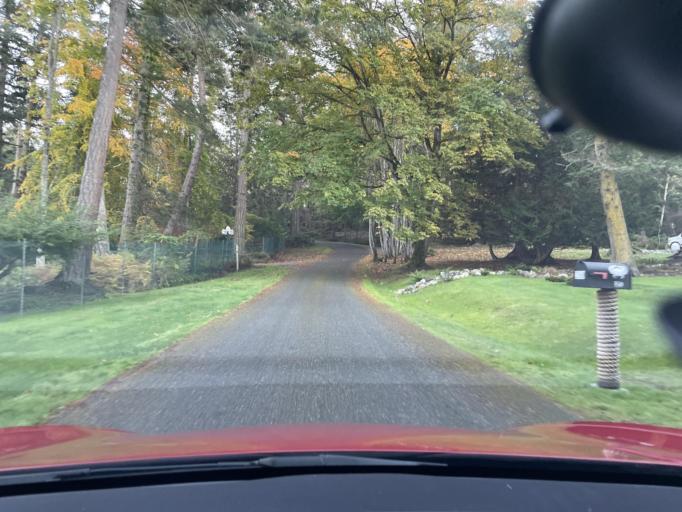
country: US
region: Washington
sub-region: San Juan County
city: Friday Harbor
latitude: 48.6195
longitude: -123.1433
